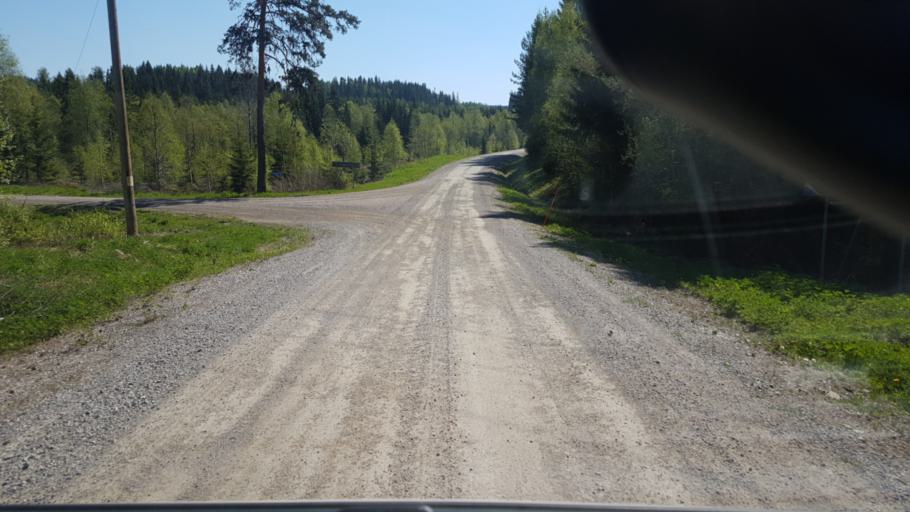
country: SE
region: Vaermland
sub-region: Arvika Kommun
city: Arvika
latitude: 59.8383
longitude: 12.7439
